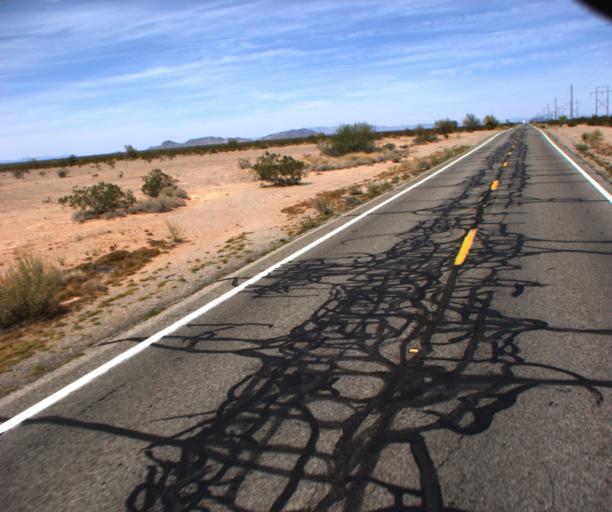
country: US
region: Arizona
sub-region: La Paz County
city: Quartzsite
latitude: 33.8378
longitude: -114.2170
